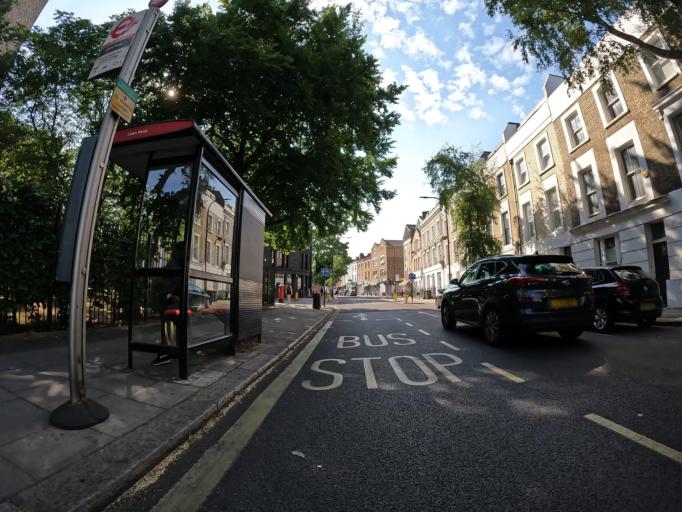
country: GB
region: England
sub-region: Greater London
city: Hendon
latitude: 51.5757
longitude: -0.1954
